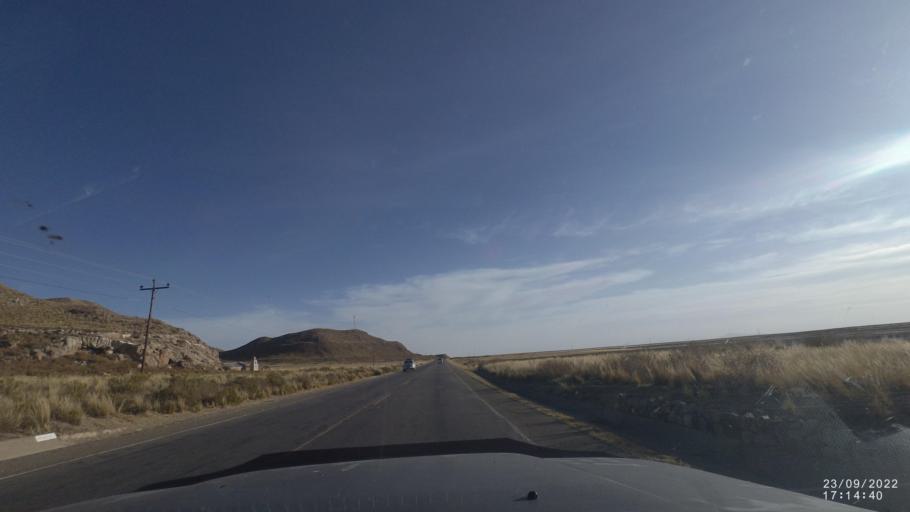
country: BO
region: Oruro
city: Challapata
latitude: -18.7249
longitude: -66.8666
